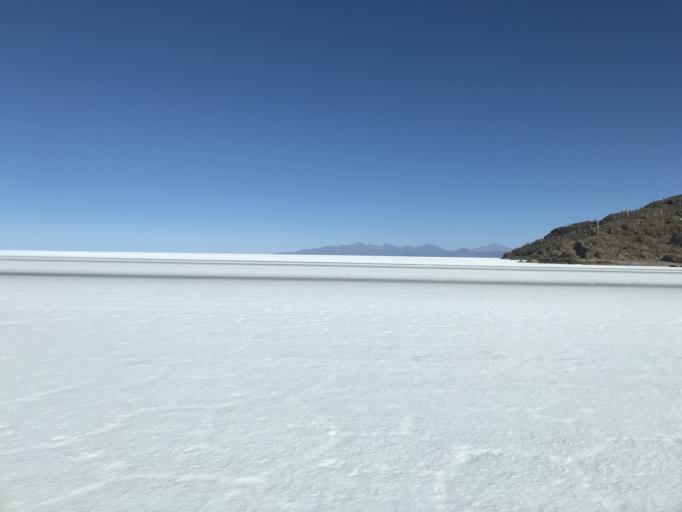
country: BO
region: Potosi
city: Colchani
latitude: -20.2381
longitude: -67.6217
